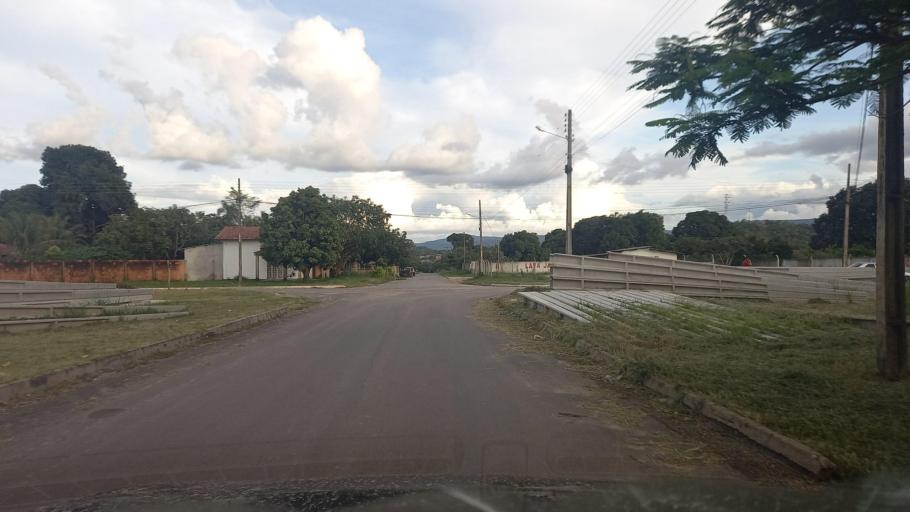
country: BR
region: Goias
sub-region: Cavalcante
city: Cavalcante
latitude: -13.7913
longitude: -47.4588
